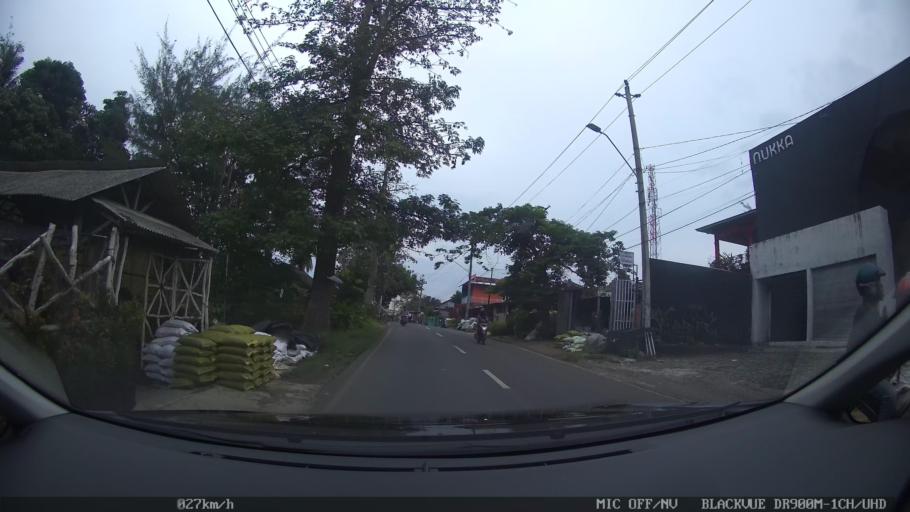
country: ID
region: Lampung
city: Kedaton
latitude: -5.3918
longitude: 105.2328
